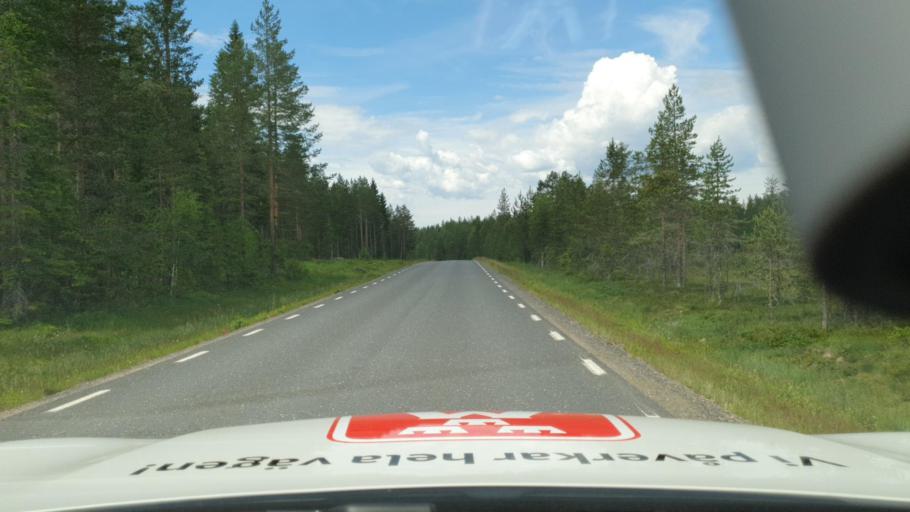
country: SE
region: Vaermland
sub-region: Torsby Kommun
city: Torsby
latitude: 60.5339
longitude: 12.8148
